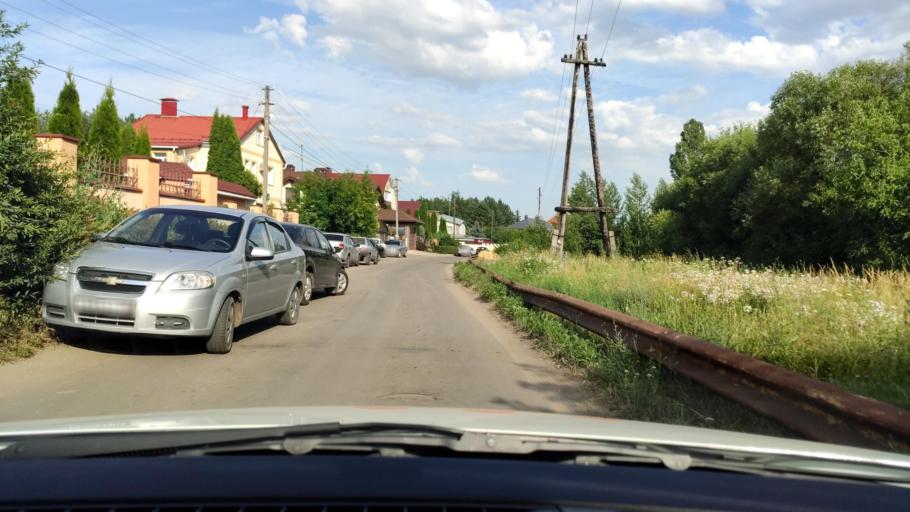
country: RU
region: Voronezj
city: Novaya Usman'
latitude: 51.6292
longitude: 39.4192
